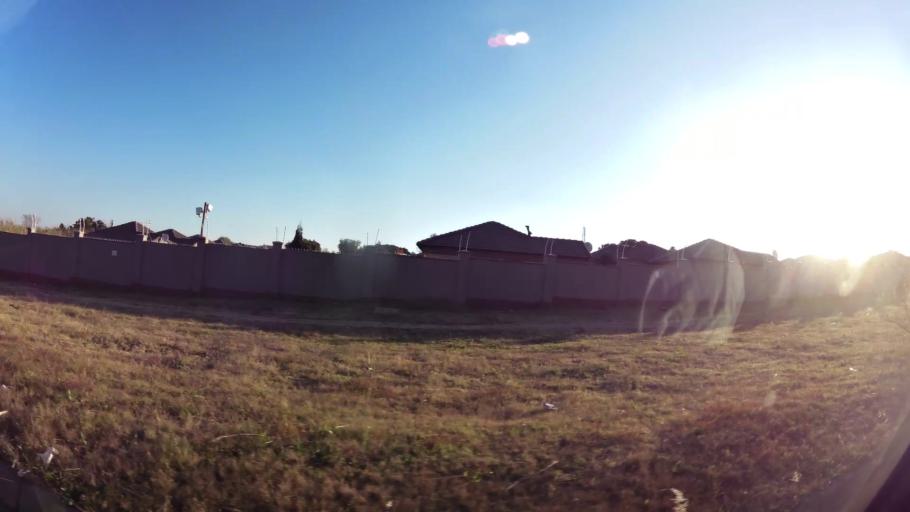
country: ZA
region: Gauteng
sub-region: City of Johannesburg Metropolitan Municipality
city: Midrand
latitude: -25.9876
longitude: 28.1214
